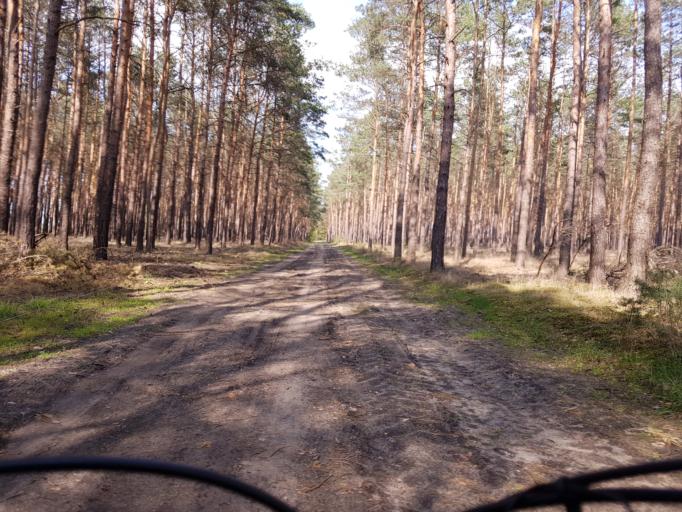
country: DE
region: Brandenburg
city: Schilda
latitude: 51.6003
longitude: 13.3796
